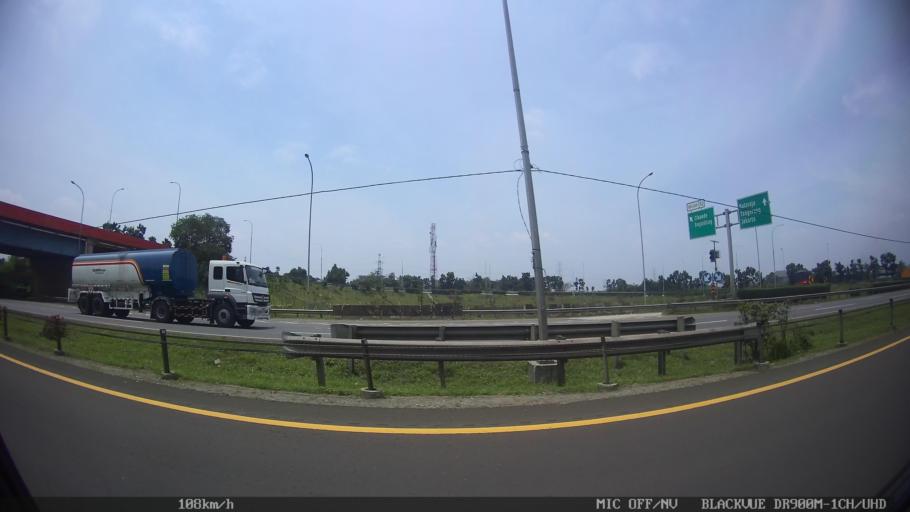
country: ID
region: West Java
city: Kresek
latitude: -6.1728
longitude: 106.3476
